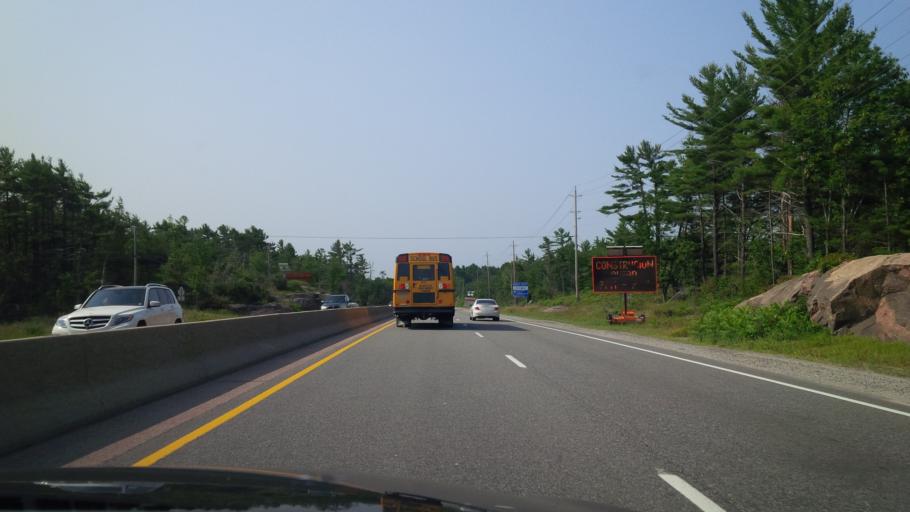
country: CA
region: Ontario
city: Gravenhurst
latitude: 44.7863
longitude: -79.3332
